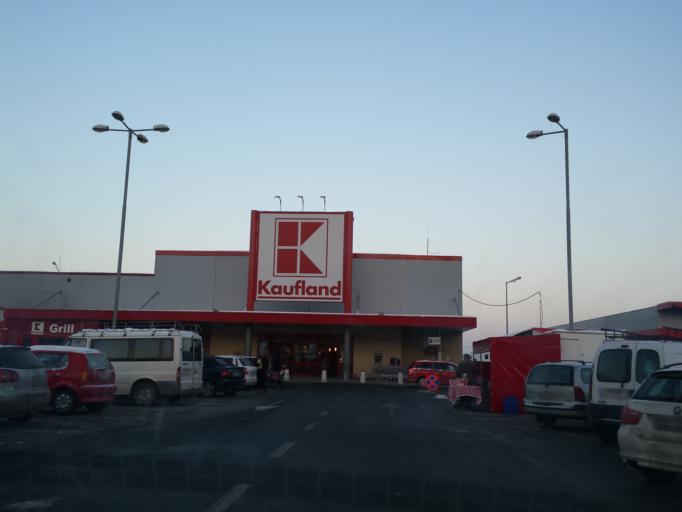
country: RO
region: Alba
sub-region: Municipiul Alba Iulia
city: Micesti
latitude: 46.0809
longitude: 23.5636
